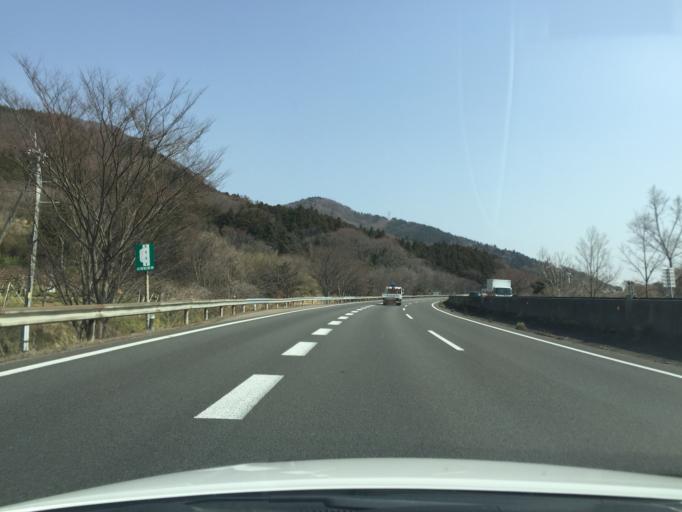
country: JP
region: Fukushima
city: Yanagawamachi-saiwaicho
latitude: 37.9007
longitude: 140.5693
